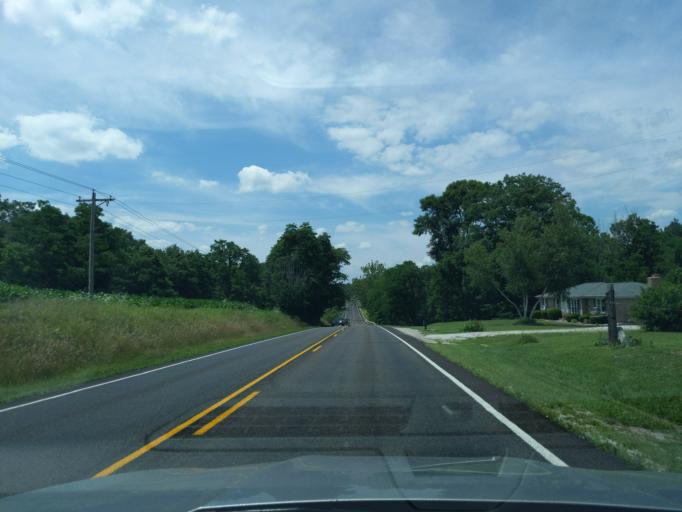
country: US
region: Indiana
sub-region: Decatur County
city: Greensburg
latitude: 39.2659
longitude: -85.3817
